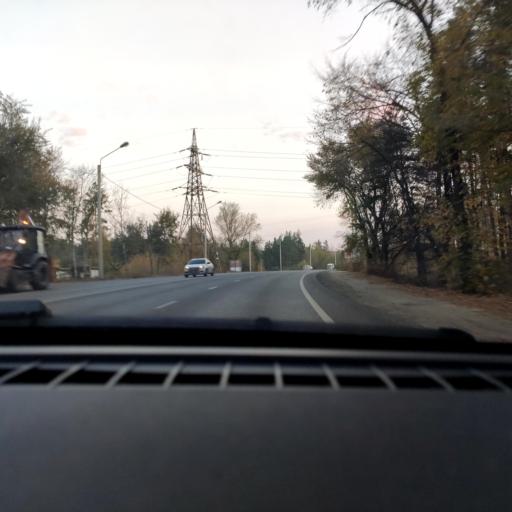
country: RU
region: Voronezj
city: Pridonskoy
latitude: 51.6784
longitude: 39.1150
